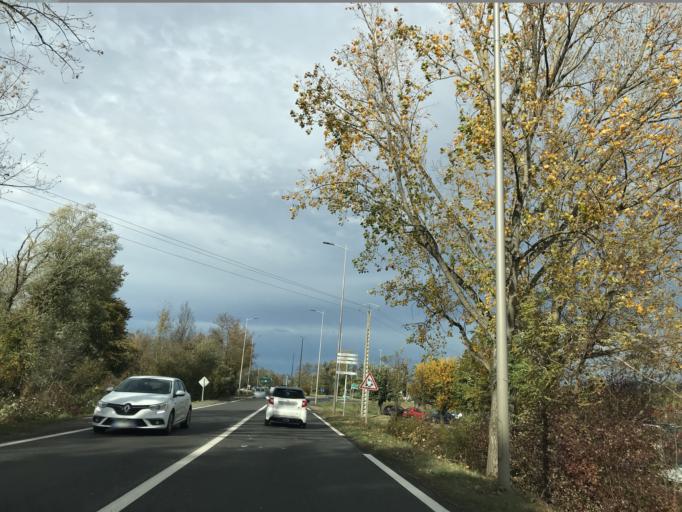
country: FR
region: Auvergne
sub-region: Departement du Puy-de-Dome
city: Peschadoires
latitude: 45.8385
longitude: 3.5065
